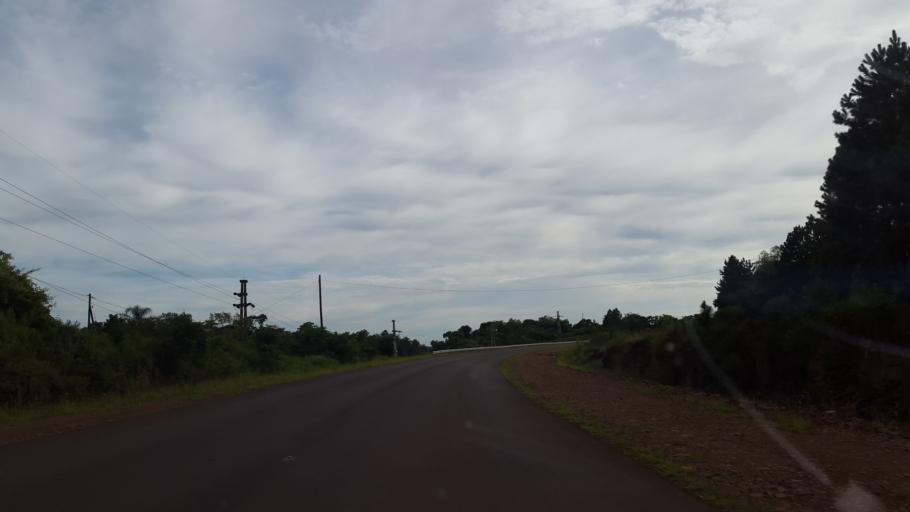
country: AR
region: Misiones
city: Bernardo de Irigoyen
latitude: -26.4226
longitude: -53.8387
